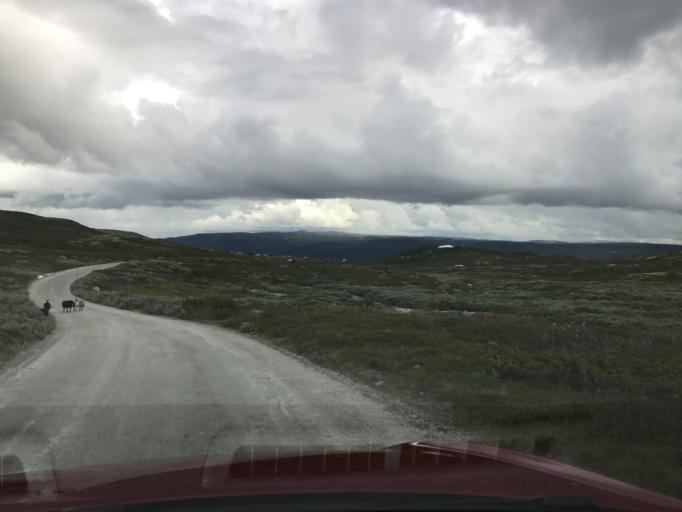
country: NO
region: Buskerud
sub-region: Hol
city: Geilo
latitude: 60.5463
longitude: 8.1536
